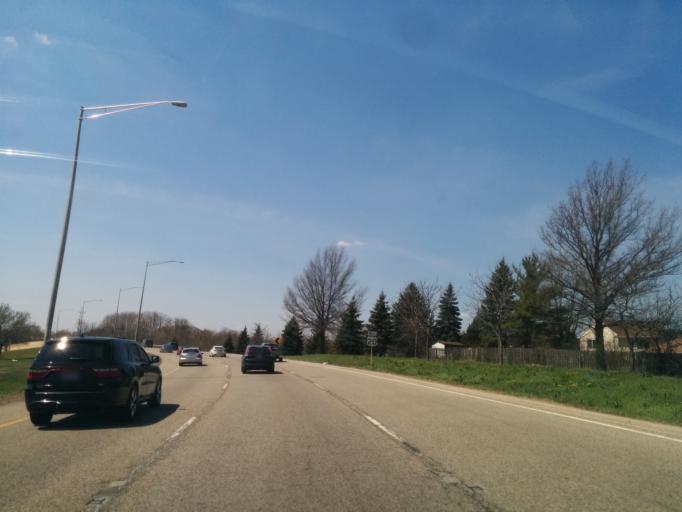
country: US
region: Illinois
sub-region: Kane County
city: Elgin
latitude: 42.0214
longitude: -88.2431
